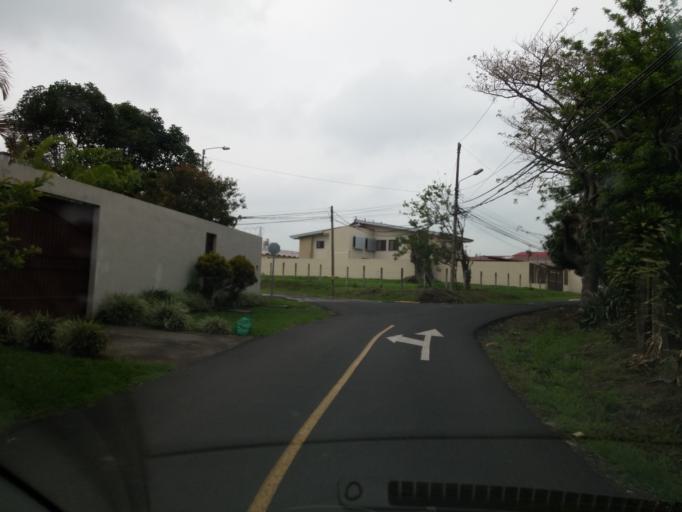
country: CR
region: Heredia
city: Mercedes
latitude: 10.0173
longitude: -84.1487
